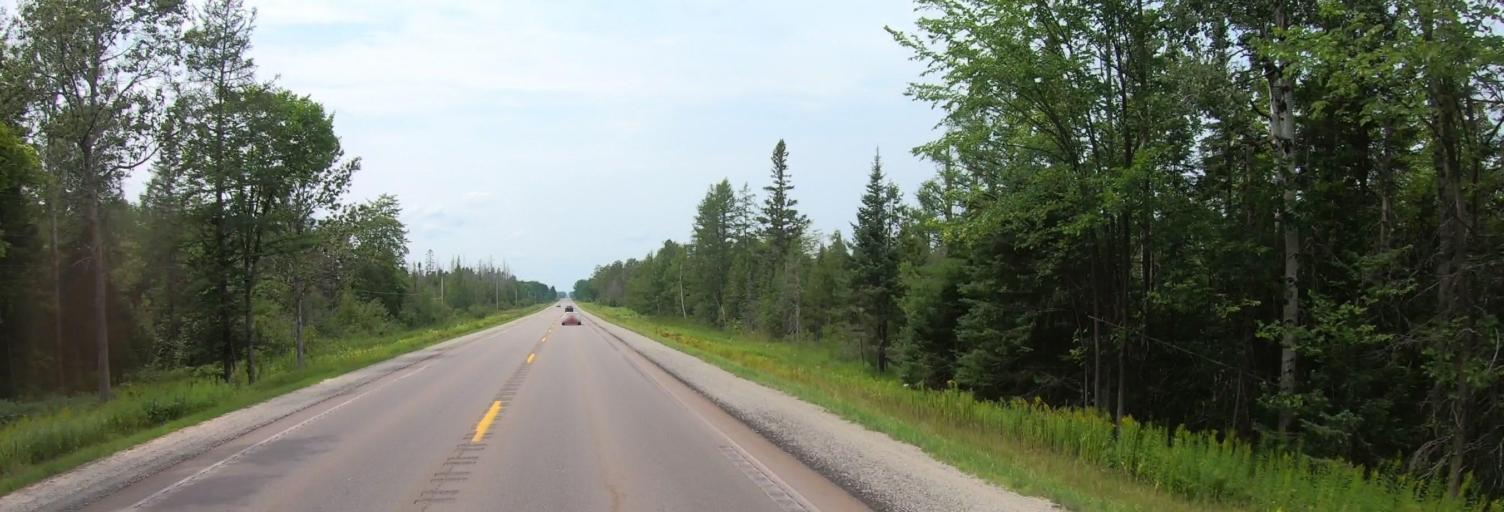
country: US
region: Michigan
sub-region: Marquette County
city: K. I. Sawyer Air Force Base
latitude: 46.3475
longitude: -87.0631
